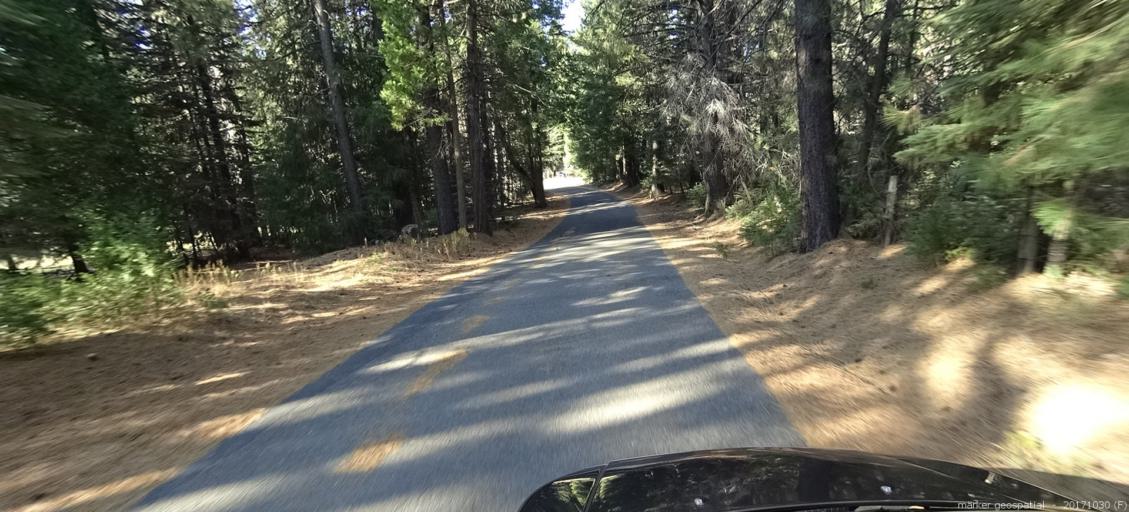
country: US
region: California
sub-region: Shasta County
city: Shingletown
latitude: 40.5372
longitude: -121.7261
